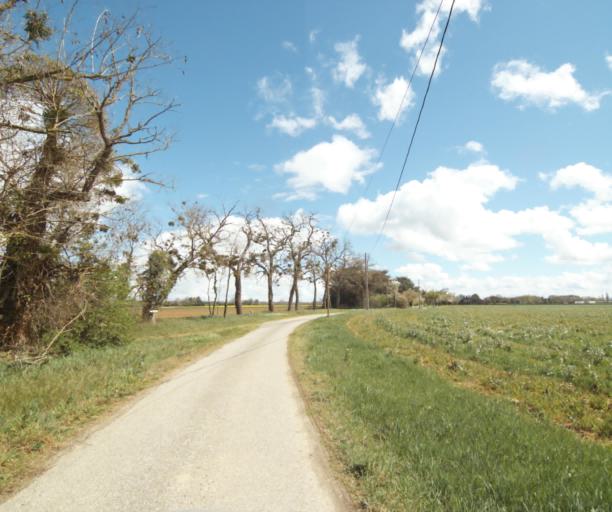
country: FR
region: Midi-Pyrenees
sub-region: Departement de l'Ariege
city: Saverdun
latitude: 43.2666
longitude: 1.5894
